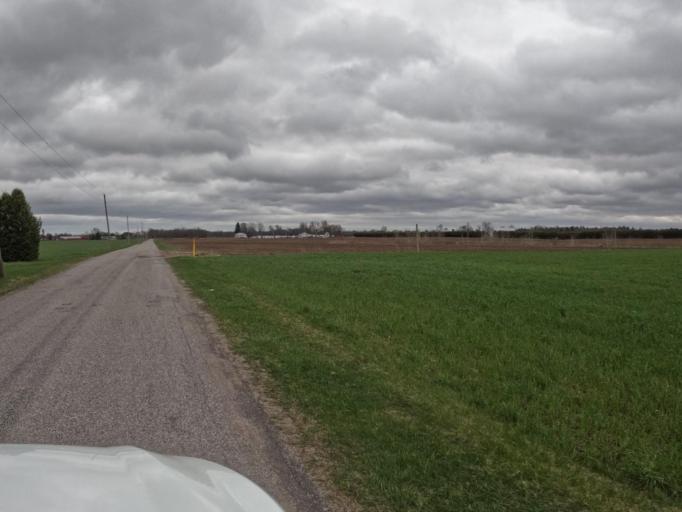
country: CA
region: Ontario
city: Norfolk County
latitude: 42.9590
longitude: -80.4264
